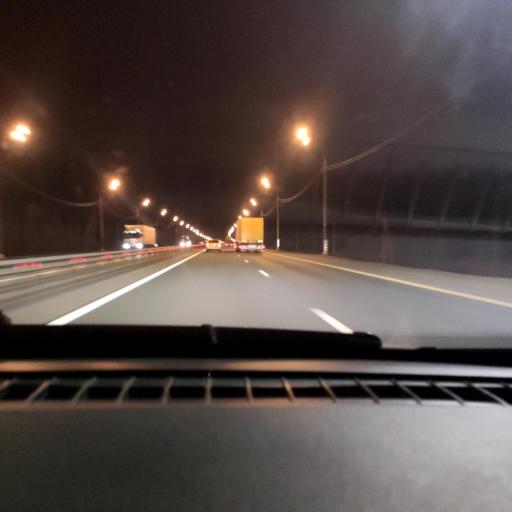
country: RU
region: Lipetsk
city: Khlevnoye
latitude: 52.2203
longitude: 39.1256
